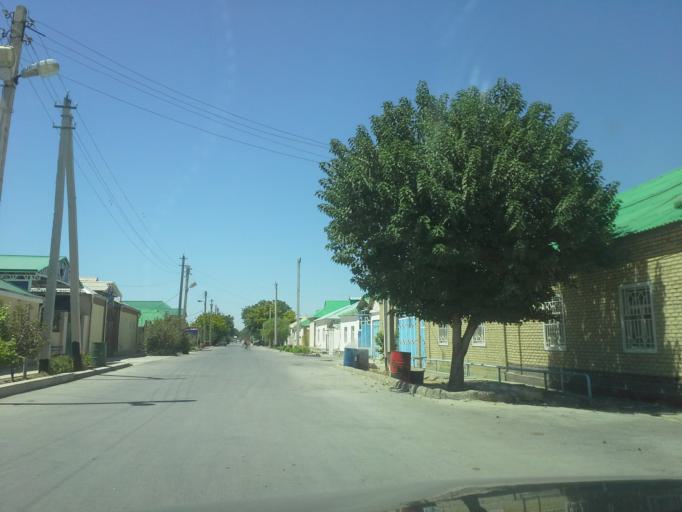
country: TM
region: Ahal
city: Abadan
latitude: 38.0404
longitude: 58.2291
